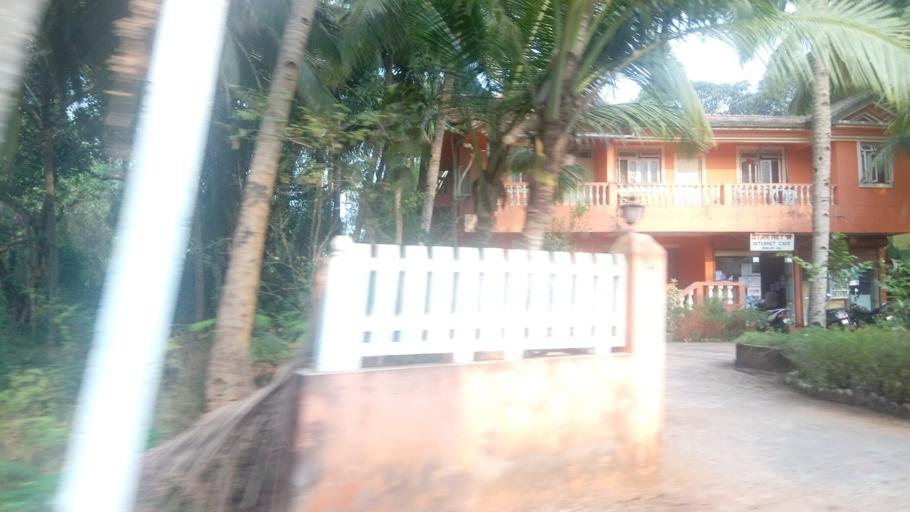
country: IN
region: Goa
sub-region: South Goa
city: Benaulim
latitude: 15.2594
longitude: 73.9308
